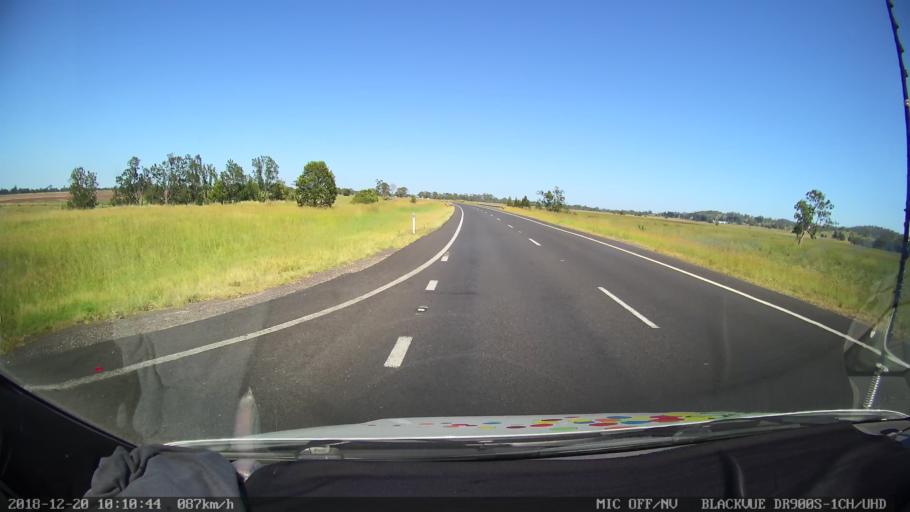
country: AU
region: New South Wales
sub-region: Richmond Valley
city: Casino
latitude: -28.8739
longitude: 153.1688
